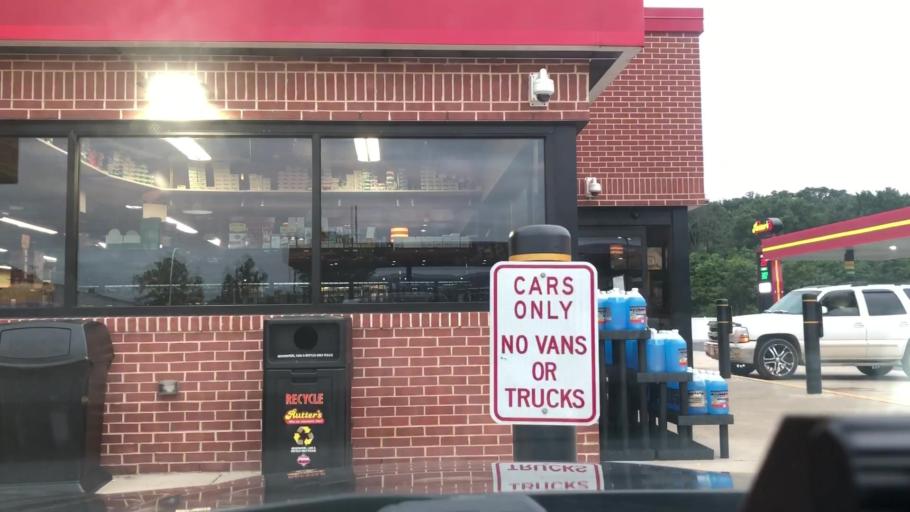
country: US
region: Pennsylvania
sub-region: Berks County
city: Hamburg
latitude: 40.5488
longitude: -75.9870
